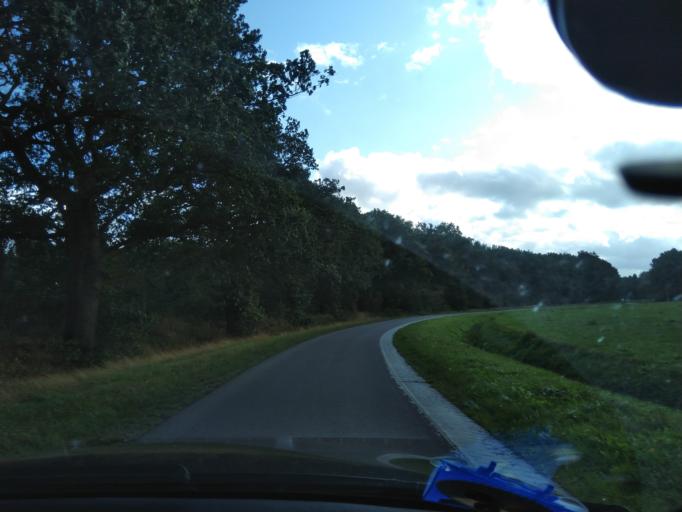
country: NL
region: Drenthe
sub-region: Gemeente Tynaarlo
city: Vries
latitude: 53.0755
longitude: 6.5479
